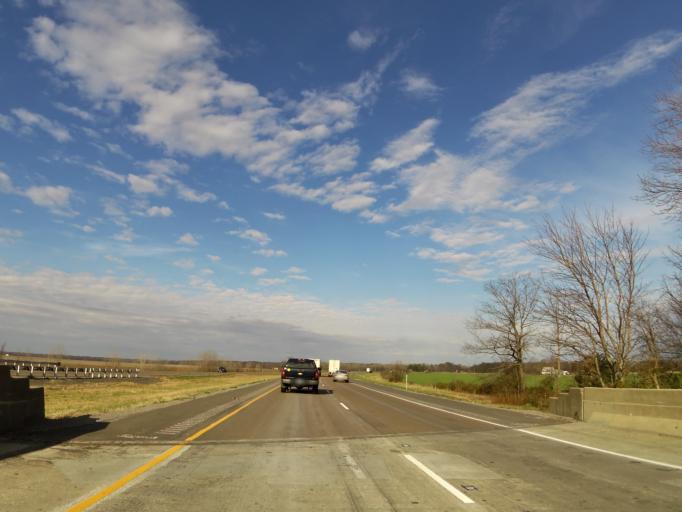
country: US
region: Illinois
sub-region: Washington County
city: Okawville
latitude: 38.4572
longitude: -89.5630
